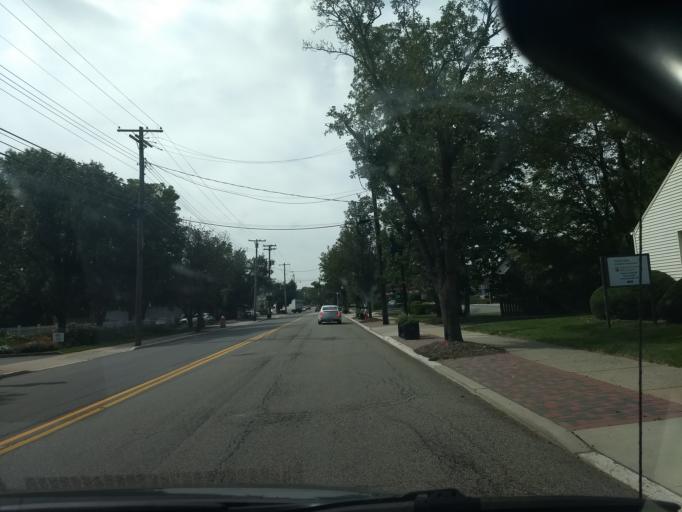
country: US
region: New Jersey
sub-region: Morris County
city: Morris Plains
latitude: 40.8234
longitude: -74.4810
